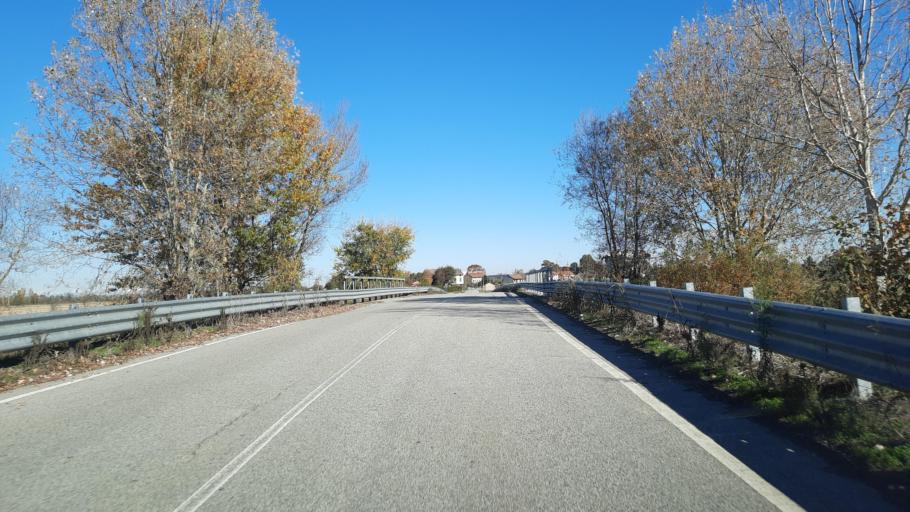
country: IT
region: Piedmont
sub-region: Provincia di Alessandria
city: Balzola
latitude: 45.1801
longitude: 8.3912
